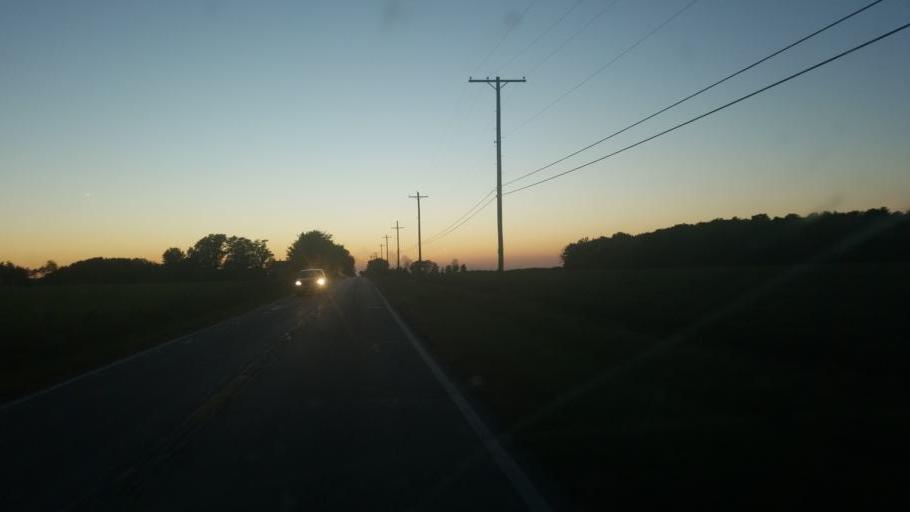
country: US
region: Ohio
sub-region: Ashtabula County
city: Jefferson
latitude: 41.7522
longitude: -80.6277
